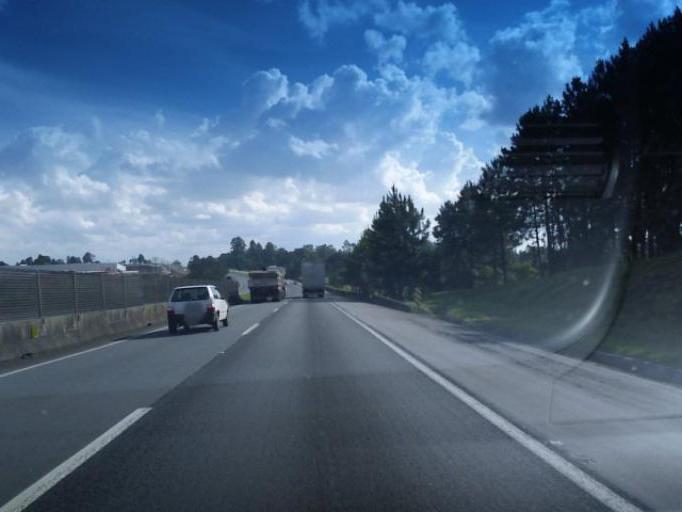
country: BR
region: Parana
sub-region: Quatro Barras
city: Quatro Barras
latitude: -25.3795
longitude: -49.0509
